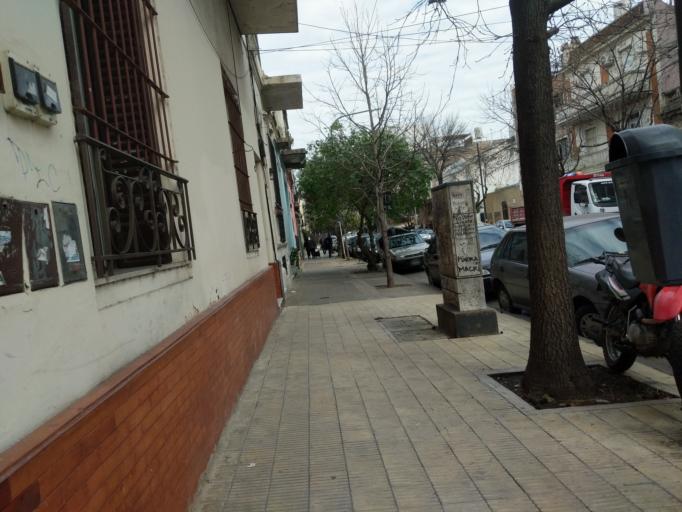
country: AR
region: Buenos Aires F.D.
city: Colegiales
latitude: -34.5854
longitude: -58.4435
